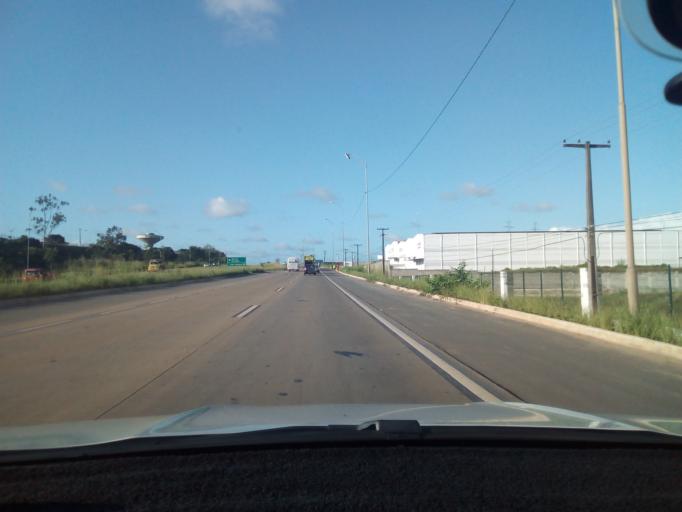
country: BR
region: Paraiba
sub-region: Conde
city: Conde
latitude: -7.2316
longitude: -34.9212
